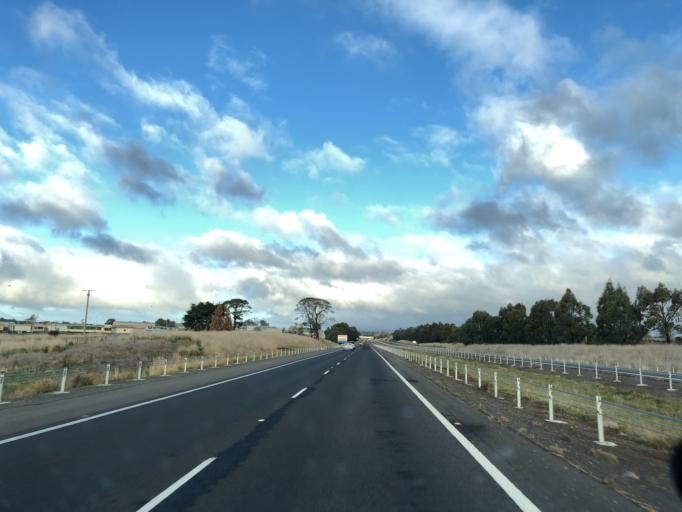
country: AU
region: Victoria
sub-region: Mount Alexander
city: Castlemaine
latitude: -37.2300
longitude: 144.4453
